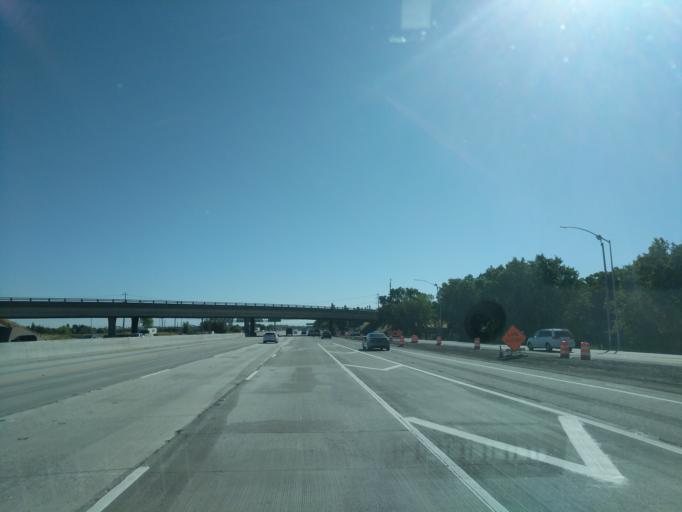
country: US
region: California
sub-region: Sacramento County
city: Sacramento
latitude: 38.6266
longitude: -121.5136
